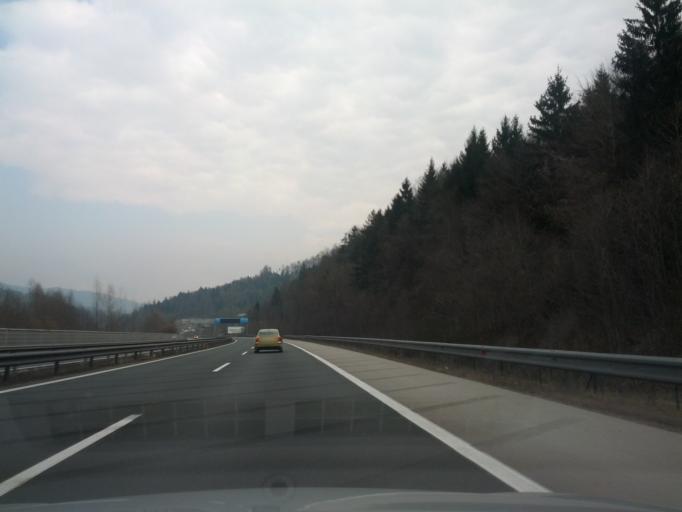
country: SI
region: Moravce
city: Moravce
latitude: 46.1647
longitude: 14.7606
